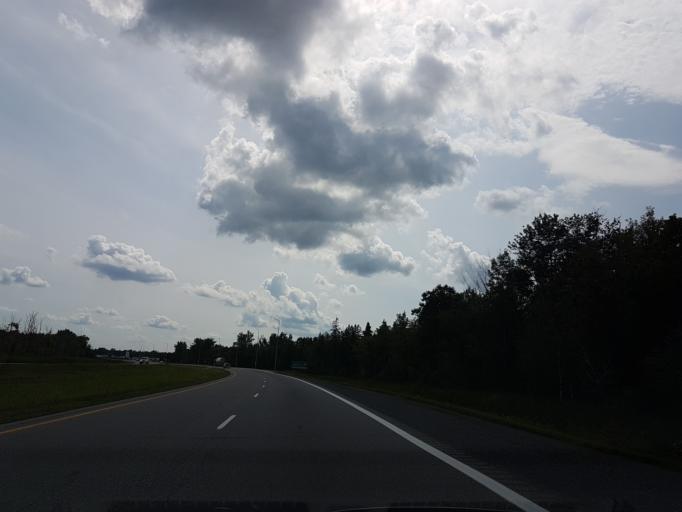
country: US
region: New York
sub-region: St. Lawrence County
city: Massena
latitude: 44.9785
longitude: -75.0773
